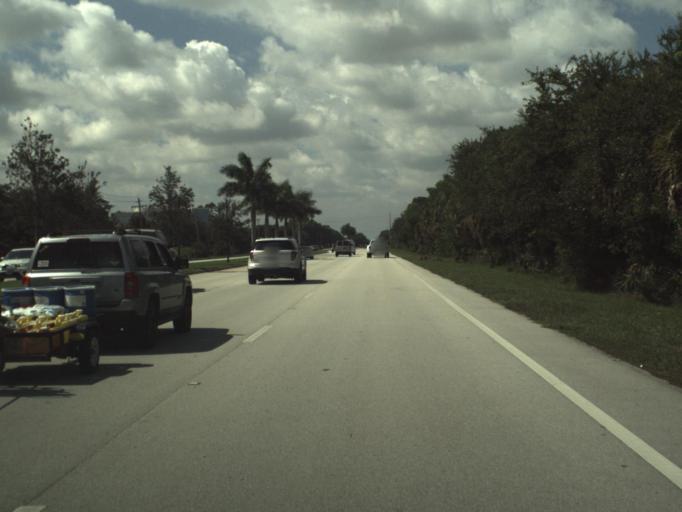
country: US
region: Florida
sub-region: Palm Beach County
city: Jupiter
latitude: 26.9186
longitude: -80.0941
